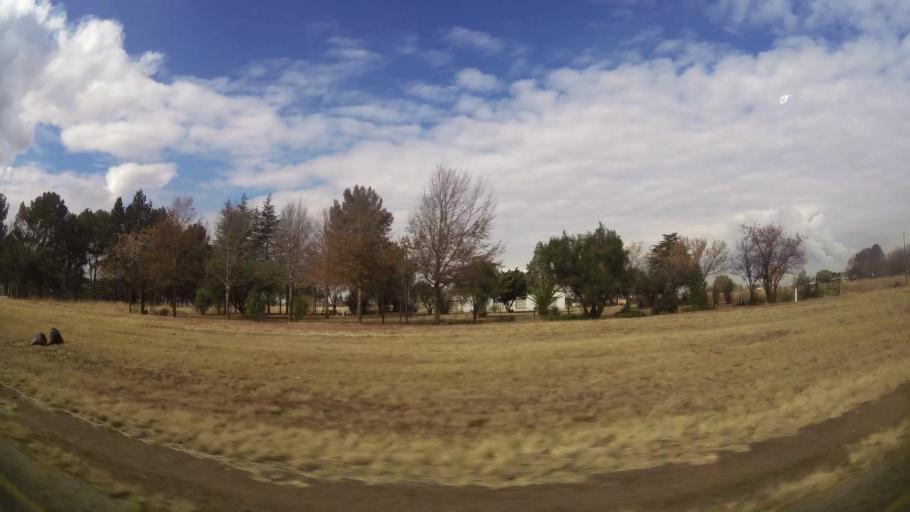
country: ZA
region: Gauteng
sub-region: Sedibeng District Municipality
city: Meyerton
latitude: -26.6437
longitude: 28.0352
